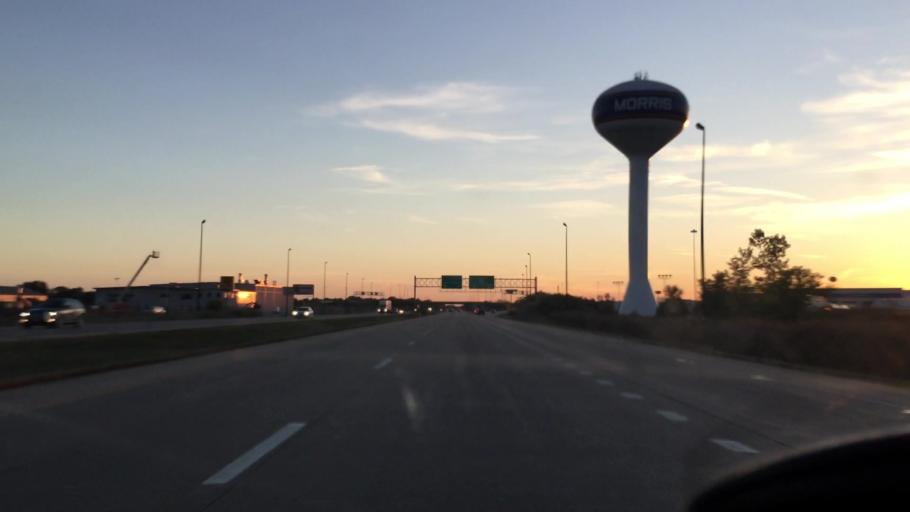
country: US
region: Illinois
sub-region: Grundy County
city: Morris
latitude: 41.3929
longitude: -88.4151
